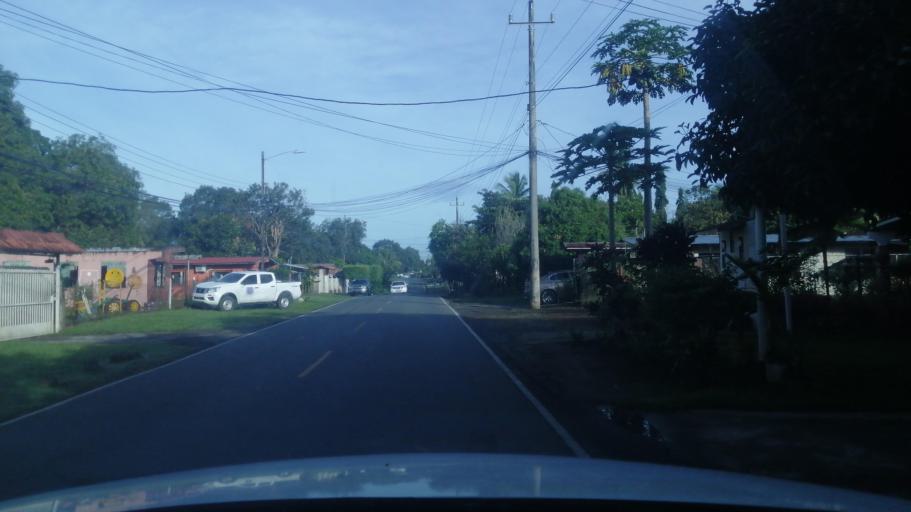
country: PA
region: Chiriqui
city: David
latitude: 8.4251
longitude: -82.4392
